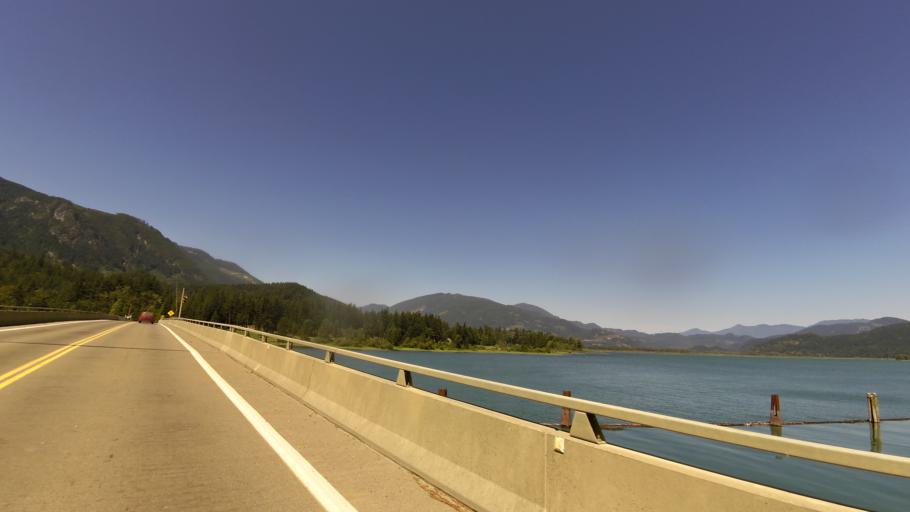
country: CA
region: British Columbia
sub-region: Fraser Valley Regional District
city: Chilliwack
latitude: 49.2463
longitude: -121.9464
